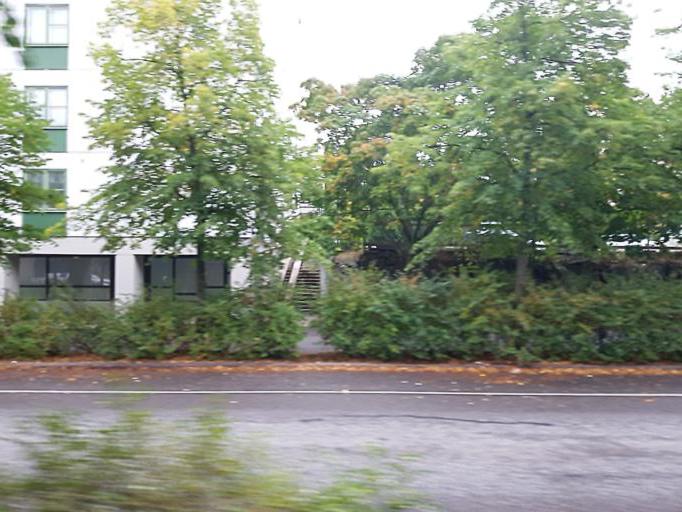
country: FI
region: Uusimaa
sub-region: Helsinki
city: Teekkarikylae
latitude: 60.2377
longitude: 24.8771
